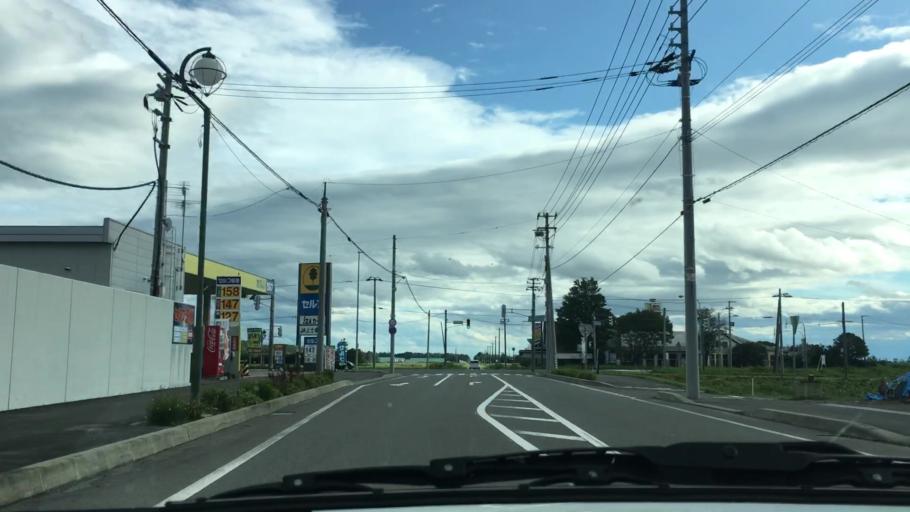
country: JP
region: Hokkaido
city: Otofuke
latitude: 43.2258
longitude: 143.2935
